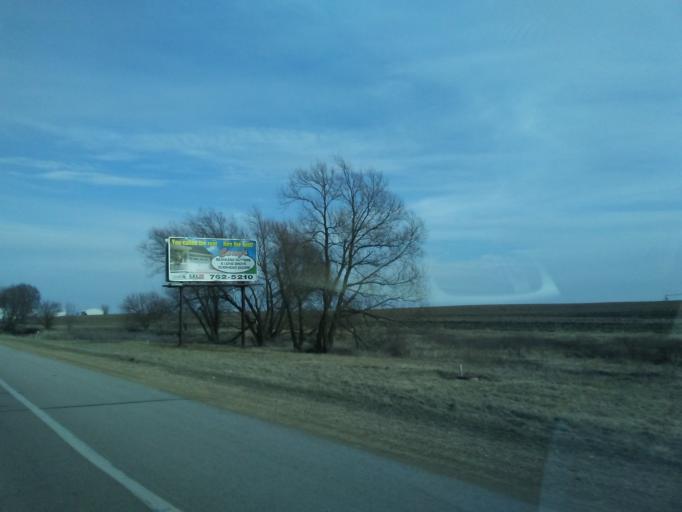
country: US
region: Wisconsin
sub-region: Iowa County
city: Mineral Point
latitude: 42.9674
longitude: -90.3271
